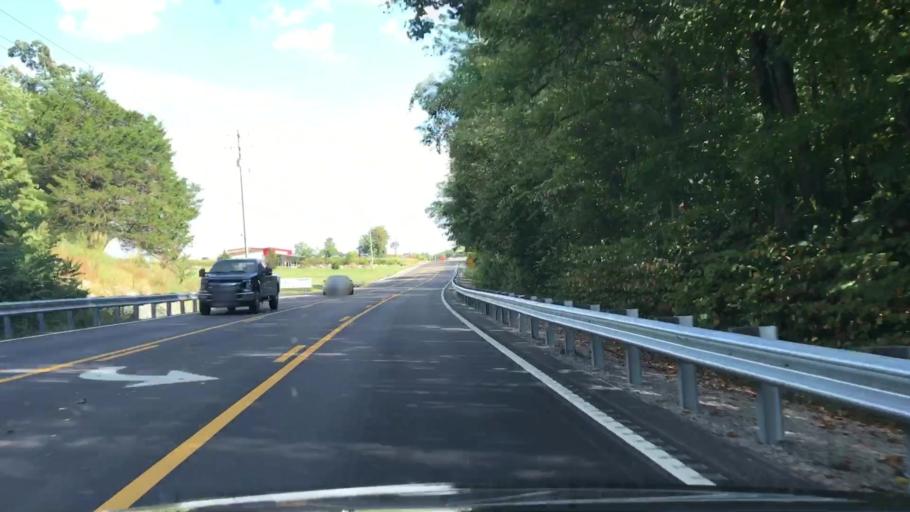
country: US
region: Alabama
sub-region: Limestone County
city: Ardmore
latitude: 35.0000
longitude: -86.8641
